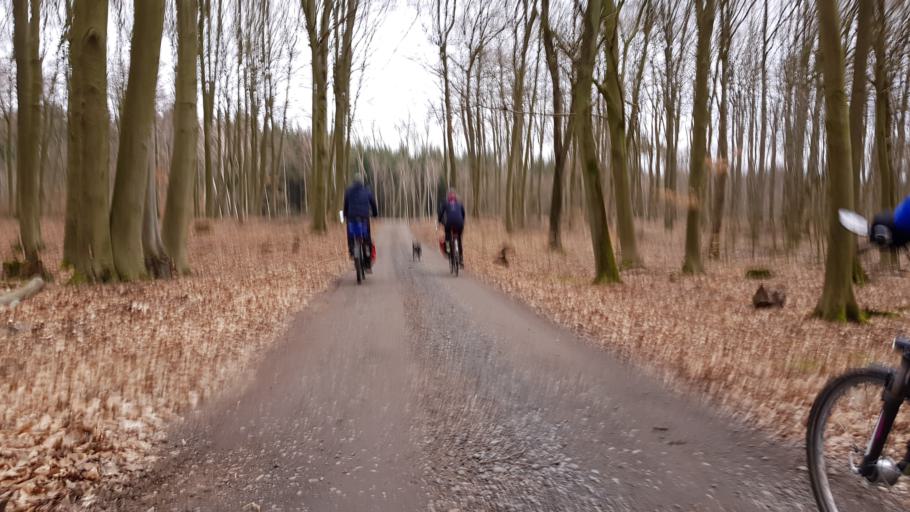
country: PL
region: West Pomeranian Voivodeship
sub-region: Powiat gryfinski
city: Banie
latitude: 53.0695
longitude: 14.7378
